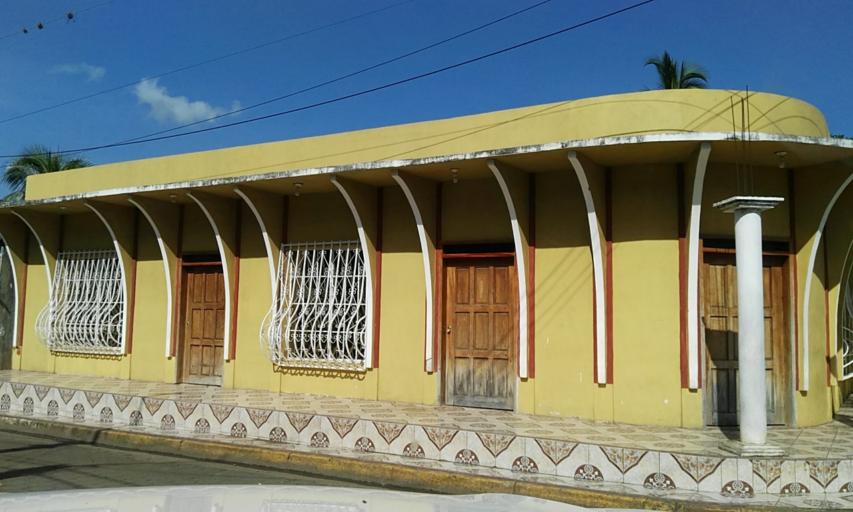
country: NI
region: Matagalpa
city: Terrabona
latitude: 12.7305
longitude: -85.9655
